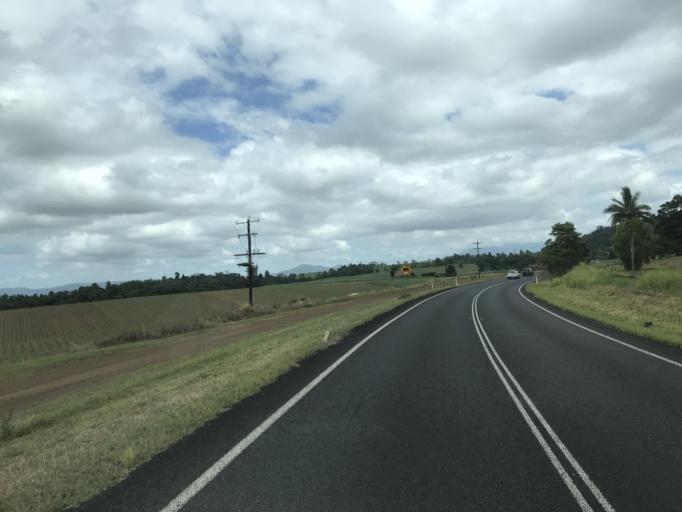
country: AU
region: Queensland
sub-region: Cassowary Coast
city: Innisfail
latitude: -17.5768
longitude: 145.9617
